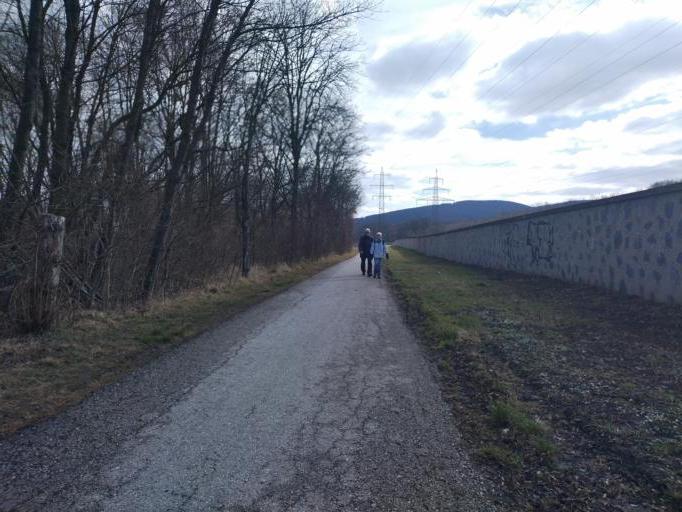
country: AT
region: Lower Austria
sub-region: Politischer Bezirk Wien-Umgebung
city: Purkersdorf
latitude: 48.2036
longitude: 16.2216
